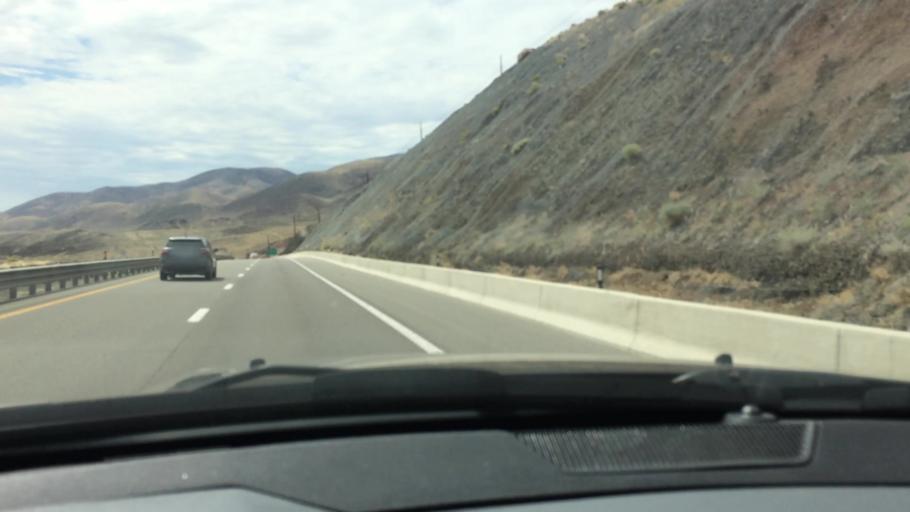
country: US
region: Nevada
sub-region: Lyon County
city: Fernley
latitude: 39.5903
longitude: -119.4031
